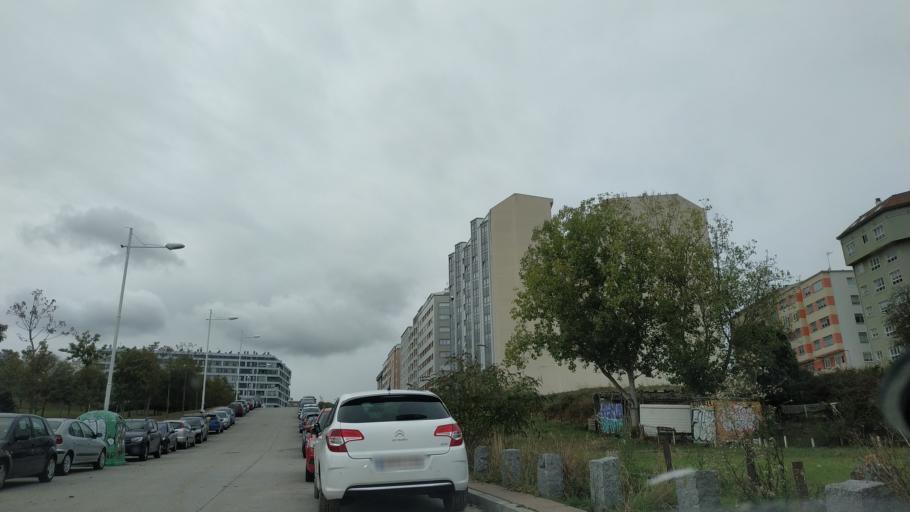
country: ES
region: Galicia
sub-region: Provincia da Coruna
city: A Coruna
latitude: 43.3479
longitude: -8.3948
